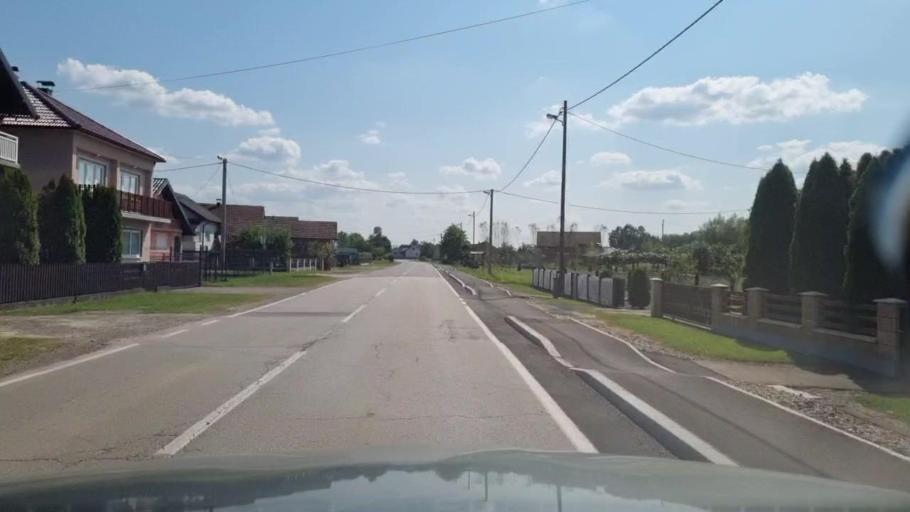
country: BA
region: Federation of Bosnia and Herzegovina
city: Odzak
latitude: 45.0294
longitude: 18.3584
